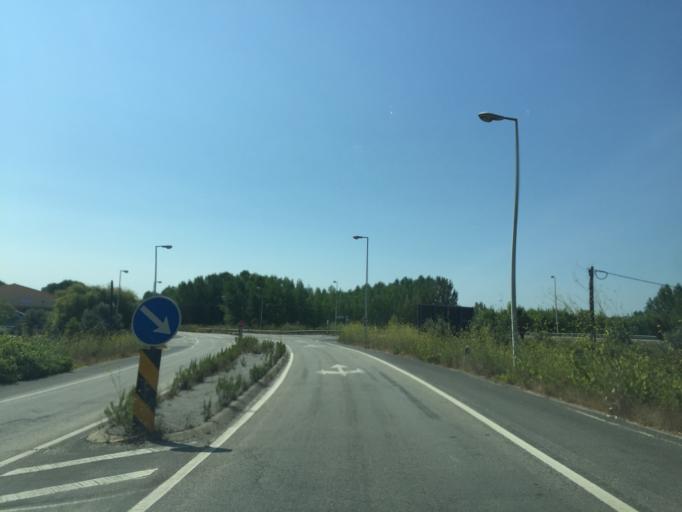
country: PT
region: Aveiro
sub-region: Mealhada
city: Mealhada
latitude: 40.3735
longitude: -8.4731
